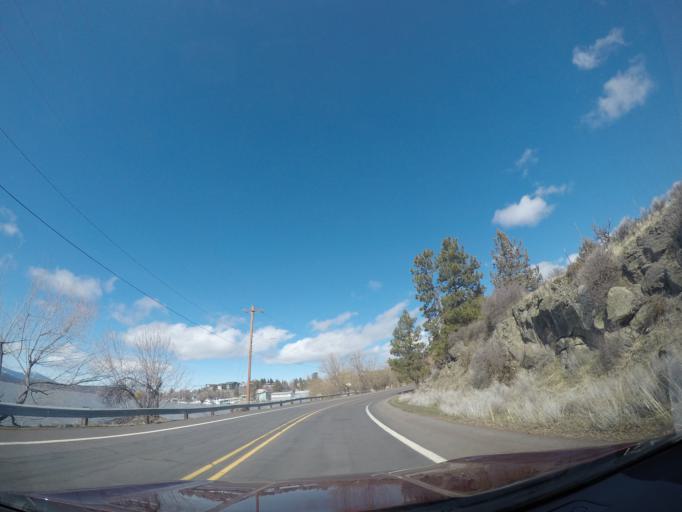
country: US
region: Oregon
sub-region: Klamath County
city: Klamath Falls
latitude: 42.2372
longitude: -121.8082
